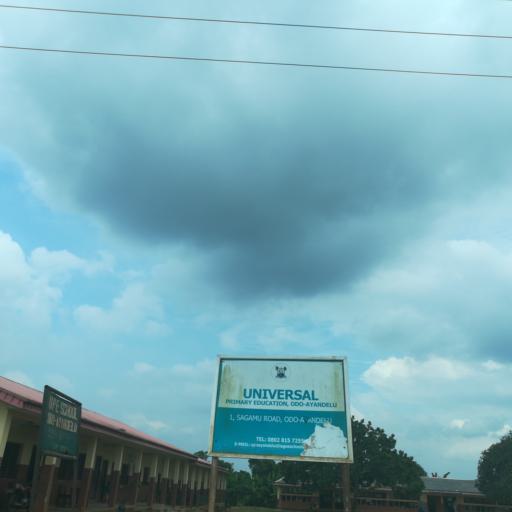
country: NG
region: Ogun
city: Odogbolu
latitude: 6.6754
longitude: 3.7122
